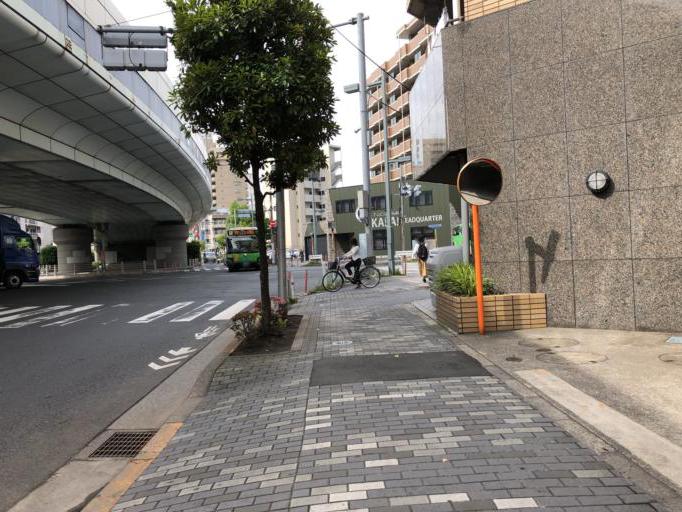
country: JP
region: Tokyo
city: Urayasu
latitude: 35.6680
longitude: 139.8734
